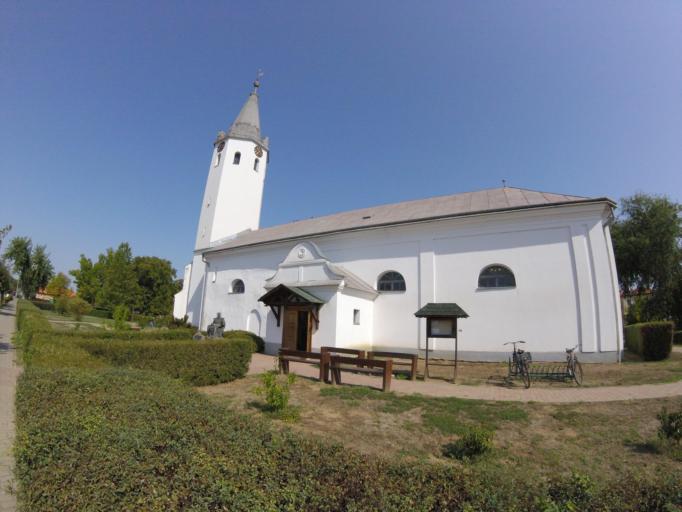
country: HU
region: Szabolcs-Szatmar-Bereg
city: Porcsalma
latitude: 47.8830
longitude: 22.5675
